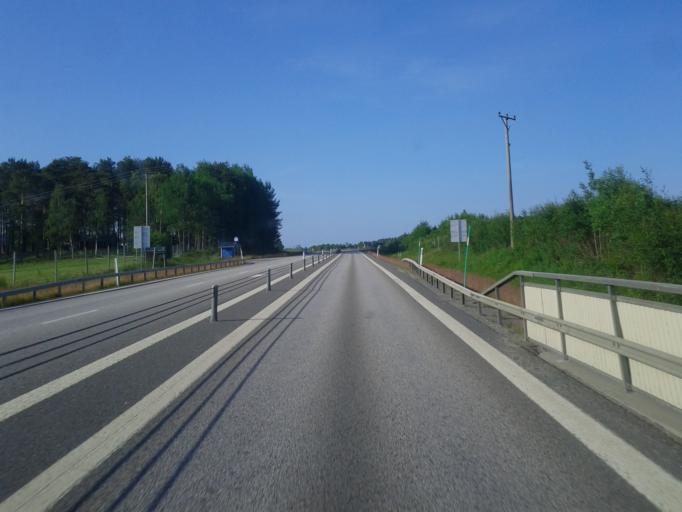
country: SE
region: Vaesterbotten
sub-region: Robertsfors Kommun
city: Robertsfors
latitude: 64.1305
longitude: 20.8899
